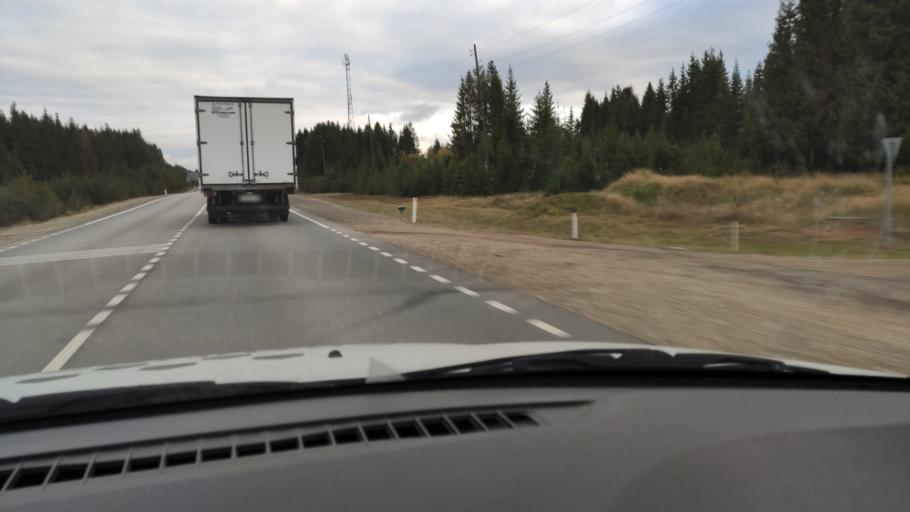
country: RU
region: Kirov
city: Chernaya Kholunitsa
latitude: 58.8566
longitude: 51.7221
